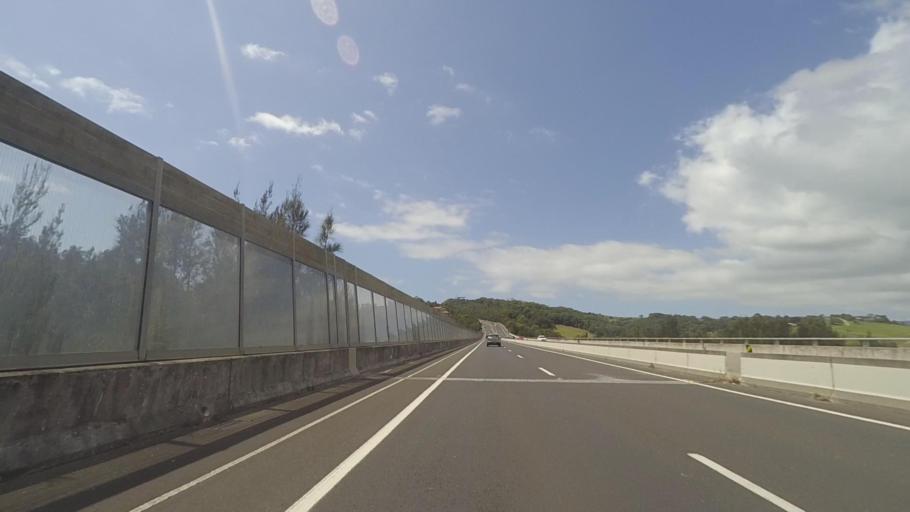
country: AU
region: New South Wales
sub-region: Kiama
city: Kiama
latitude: -34.6416
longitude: 150.8331
